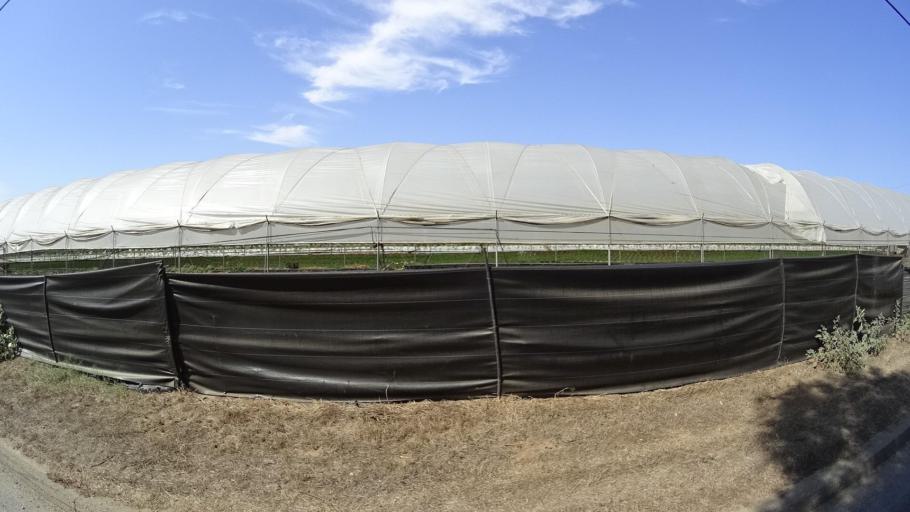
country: US
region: California
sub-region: San Diego County
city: Hidden Meadows
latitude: 33.2102
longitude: -117.1707
